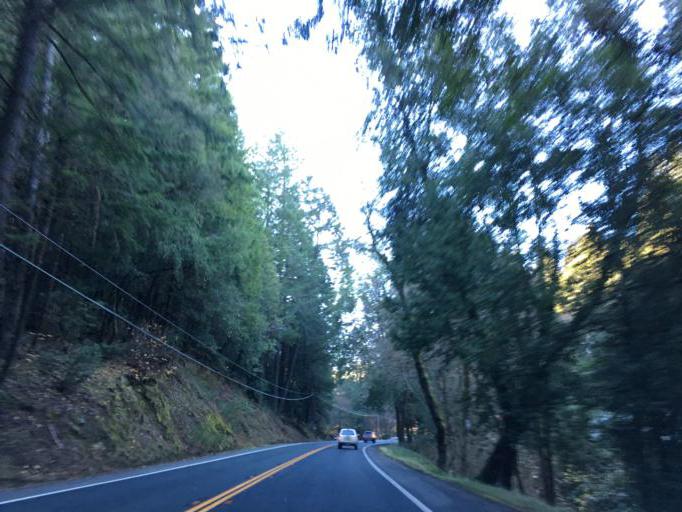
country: US
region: California
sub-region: Mendocino County
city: Brooktrails
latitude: 39.5091
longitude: -123.3842
